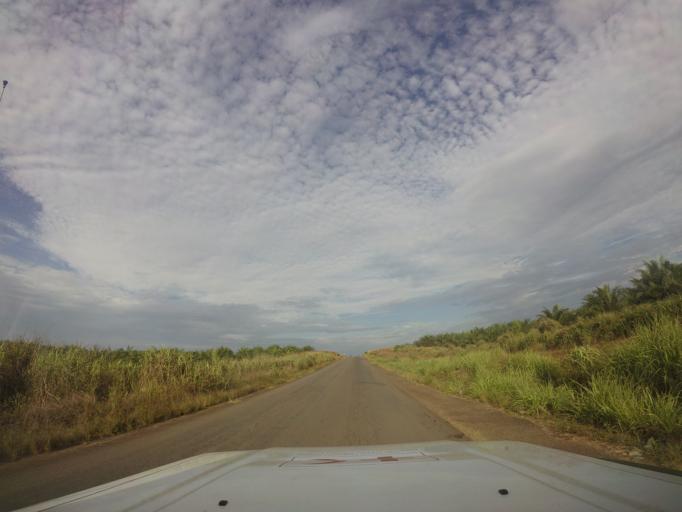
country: LR
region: Bomi
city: Tubmanburg
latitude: 6.7278
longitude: -11.0329
